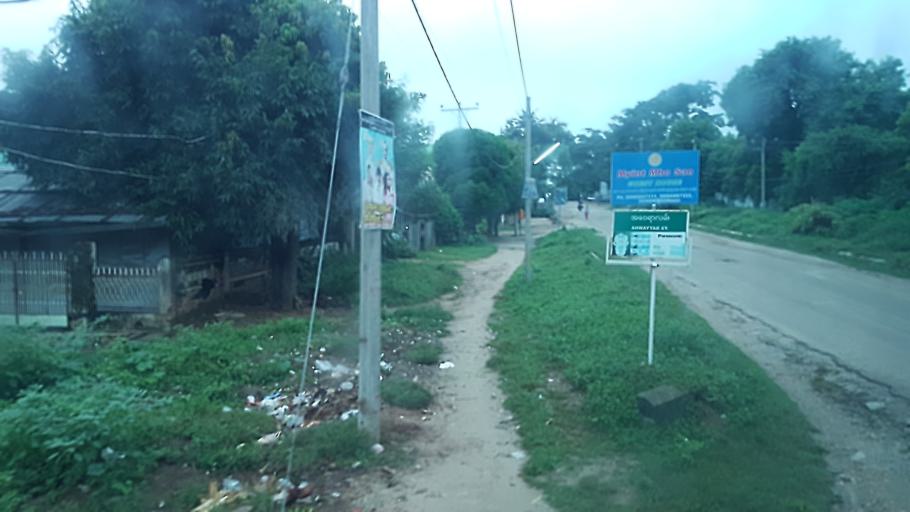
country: MM
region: Magway
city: Magway
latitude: 20.1541
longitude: 94.9406
